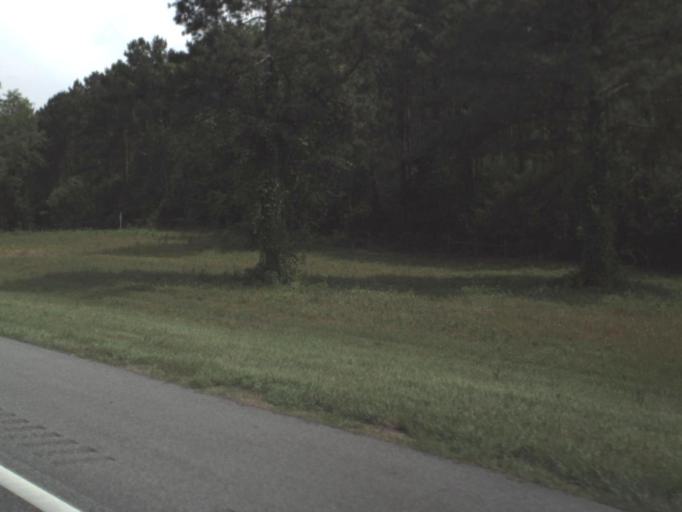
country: US
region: Florida
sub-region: Suwannee County
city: Live Oak
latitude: 30.3448
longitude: -82.9833
